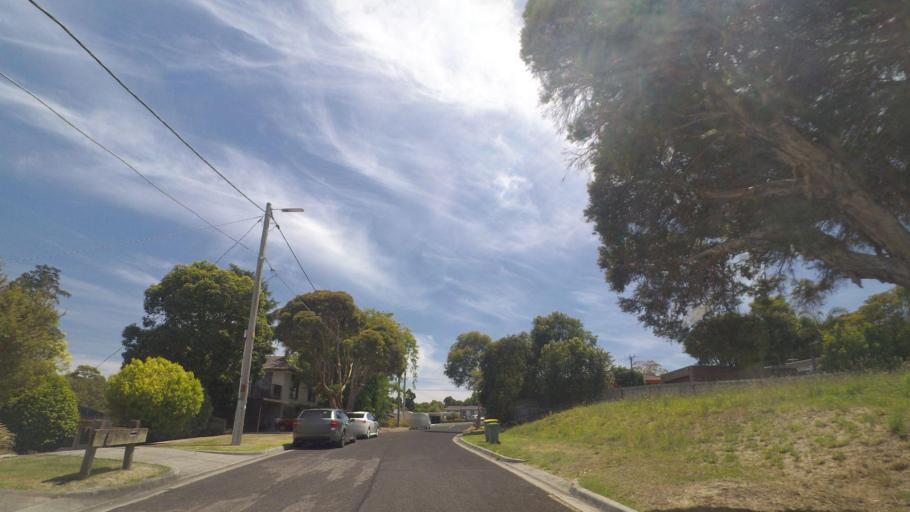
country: AU
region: Victoria
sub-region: Maroondah
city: Croydon North
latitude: -37.7721
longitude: 145.3197
